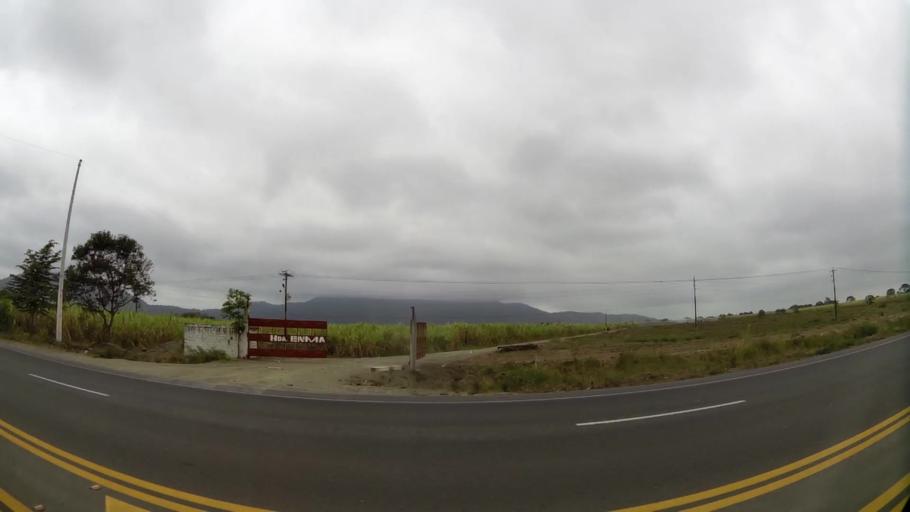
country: EC
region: Guayas
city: Naranjal
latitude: -2.4889
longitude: -79.6094
